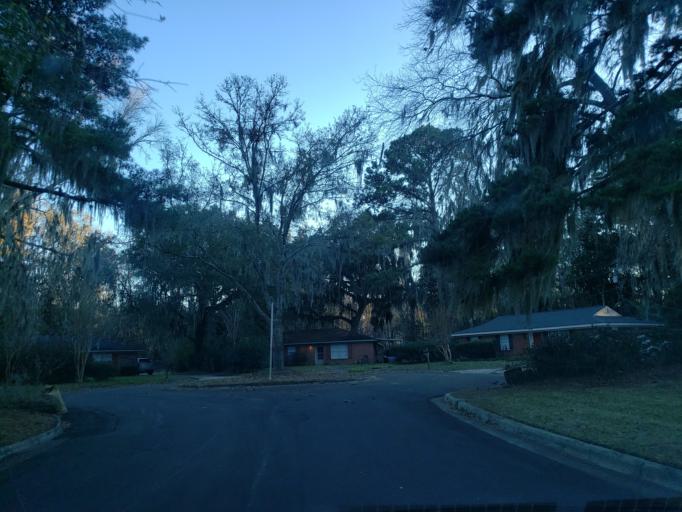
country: US
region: Georgia
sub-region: Chatham County
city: Isle of Hope
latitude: 31.9763
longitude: -81.0992
